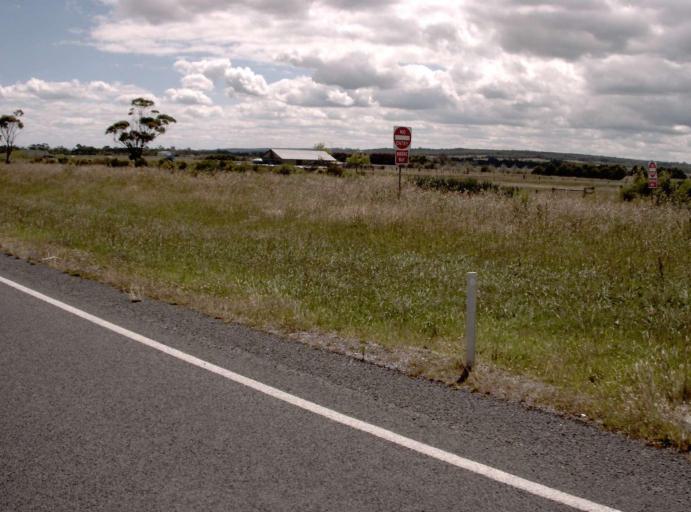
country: AU
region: Victoria
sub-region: Bass Coast
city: North Wonthaggi
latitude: -38.4530
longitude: 145.4809
